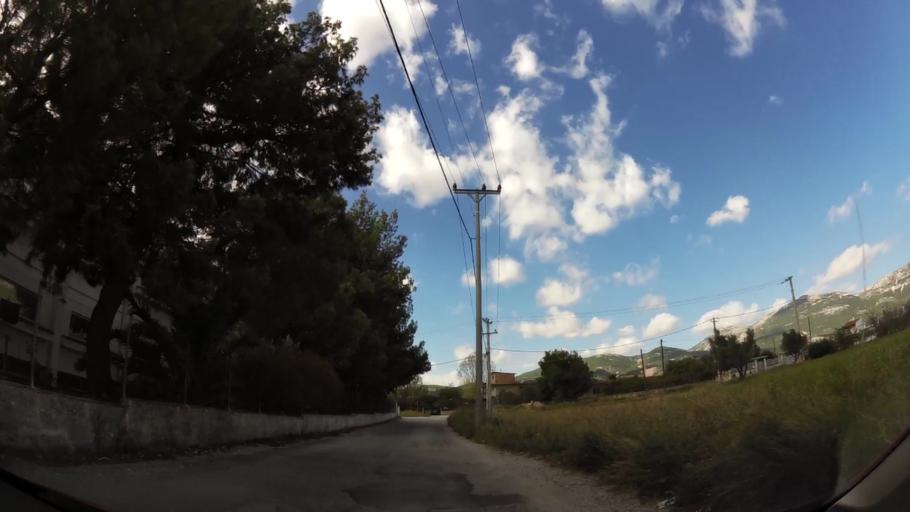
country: GR
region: Attica
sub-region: Nomarchia Anatolikis Attikis
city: Thrakomakedones
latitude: 38.1060
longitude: 23.7570
